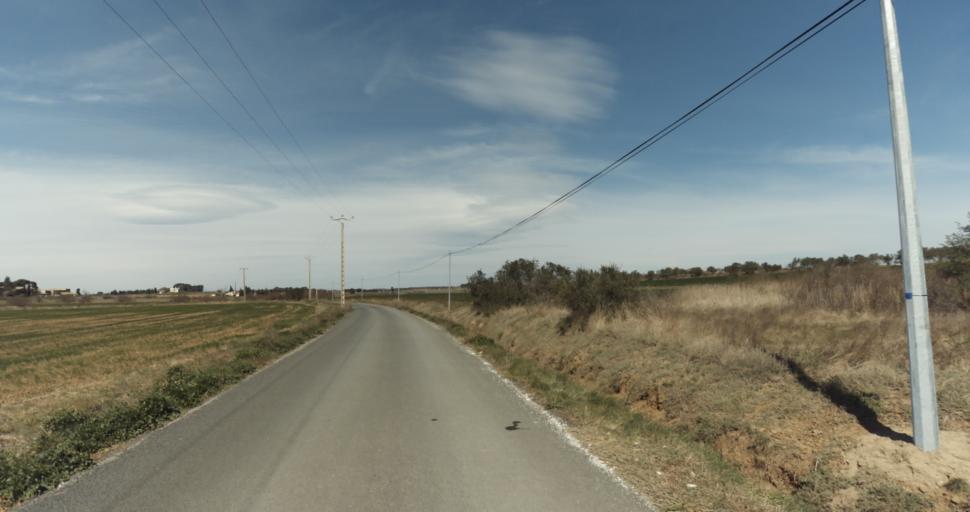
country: FR
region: Languedoc-Roussillon
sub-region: Departement de l'Herault
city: Marseillan
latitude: 43.3844
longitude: 3.5525
